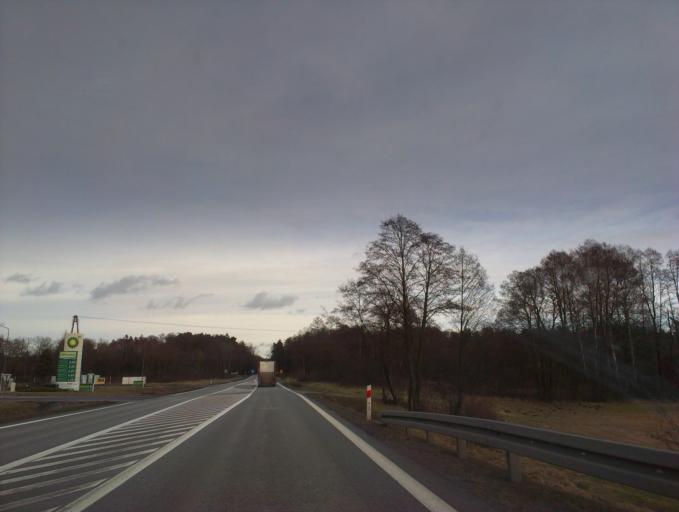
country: PL
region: Kujawsko-Pomorskie
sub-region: Powiat lipnowski
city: Skepe
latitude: 52.8818
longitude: 19.3840
